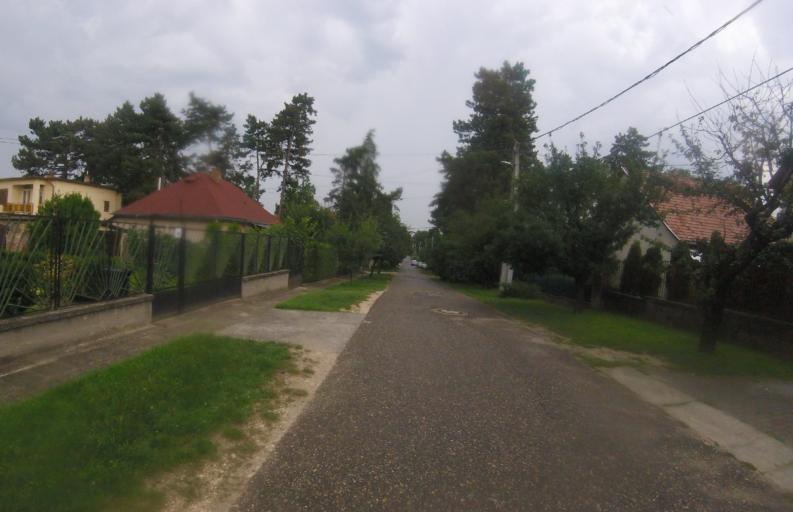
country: HU
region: Pest
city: God
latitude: 47.6759
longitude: 19.1384
